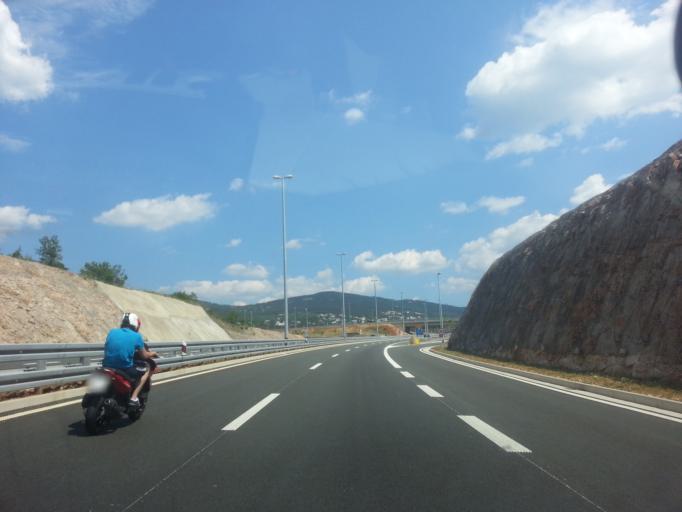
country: HR
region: Primorsko-Goranska
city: Hreljin
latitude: 45.2895
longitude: 14.5829
